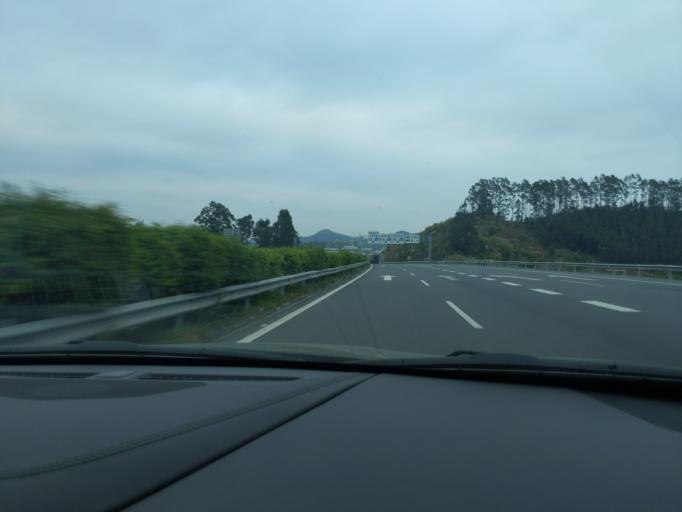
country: CN
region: Fujian
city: Neikeng
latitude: 24.7852
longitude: 118.4817
